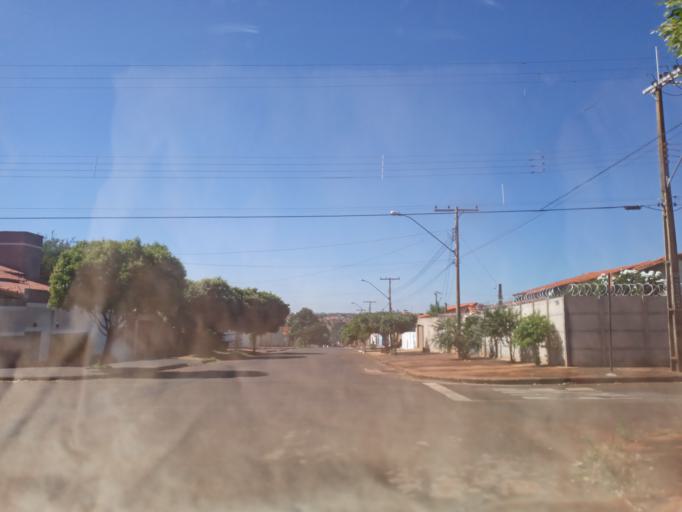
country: BR
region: Minas Gerais
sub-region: Ituiutaba
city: Ituiutaba
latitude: -18.9898
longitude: -49.4488
